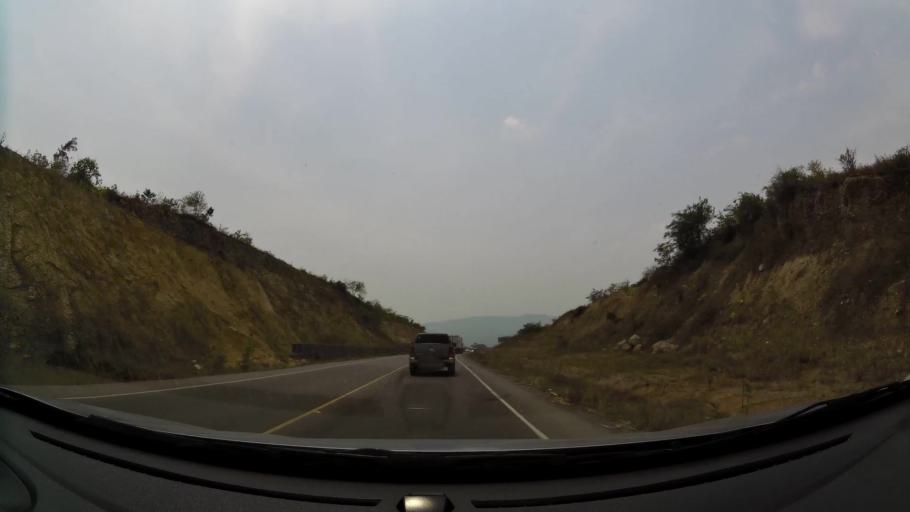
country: HN
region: Cortes
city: El Plan
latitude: 15.2646
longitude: -87.9656
